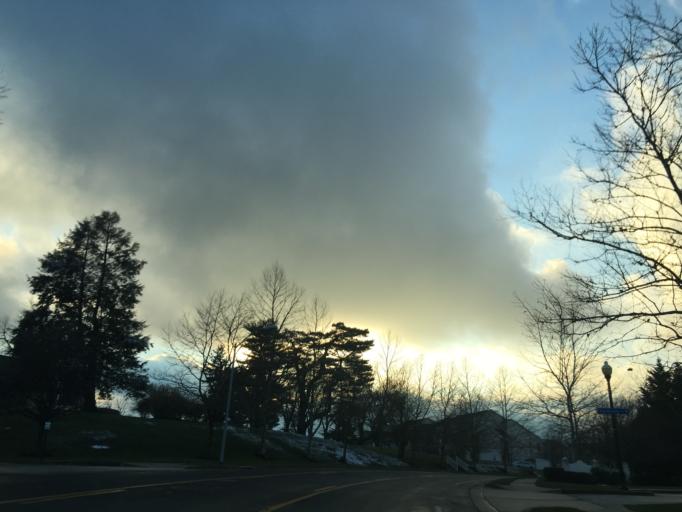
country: US
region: Maryland
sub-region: Baltimore County
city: Garrison
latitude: 39.3951
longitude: -76.7427
